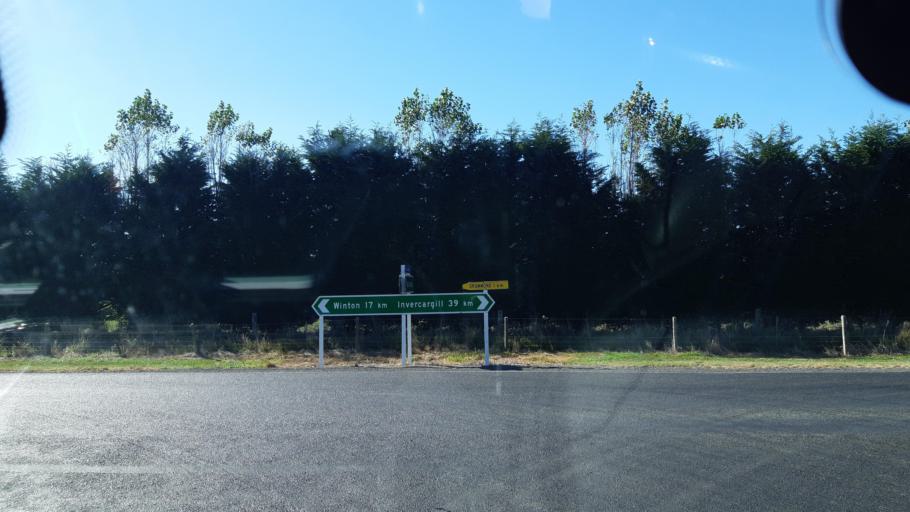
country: NZ
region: Southland
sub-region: Southland District
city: Winton
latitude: -46.1583
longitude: 168.1505
